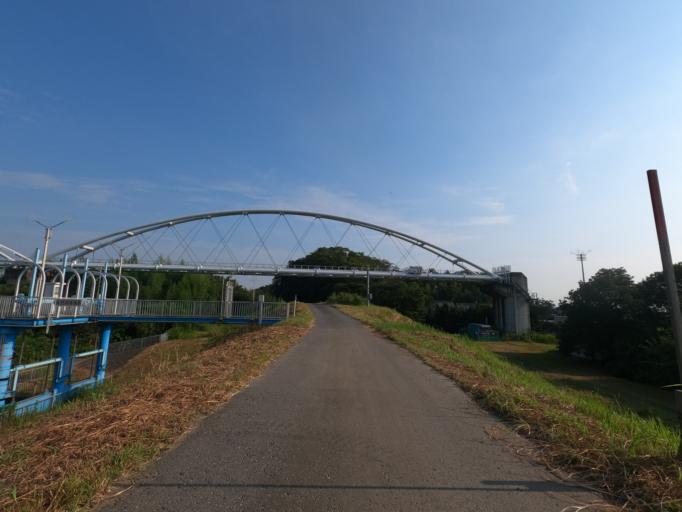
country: JP
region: Ibaraki
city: Mitsukaido
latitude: 36.0032
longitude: 139.9741
